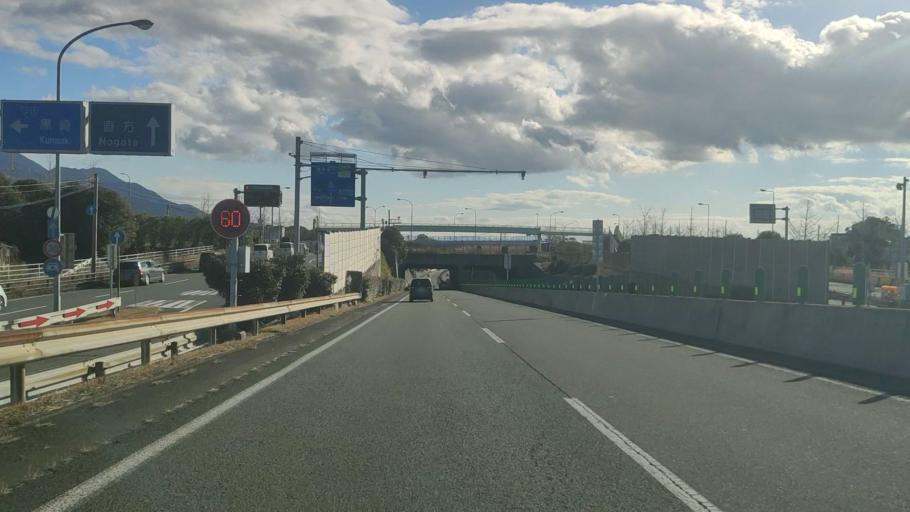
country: JP
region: Fukuoka
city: Nakama
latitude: 33.7940
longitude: 130.7444
